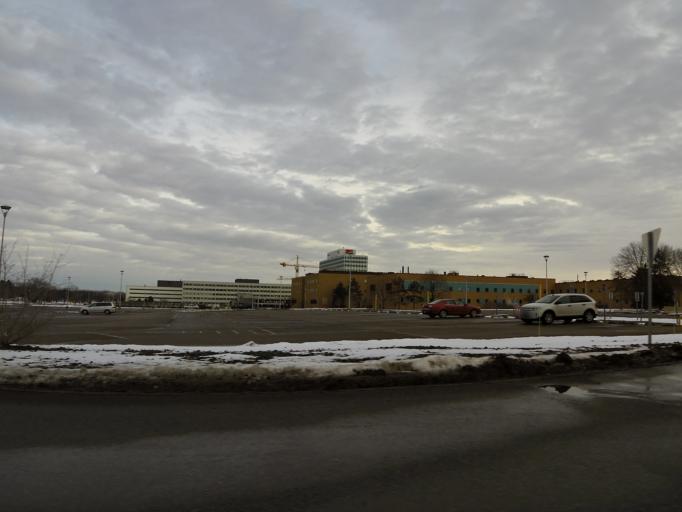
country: US
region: Minnesota
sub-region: Ramsey County
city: Maplewood
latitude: 44.9522
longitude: -93.0028
